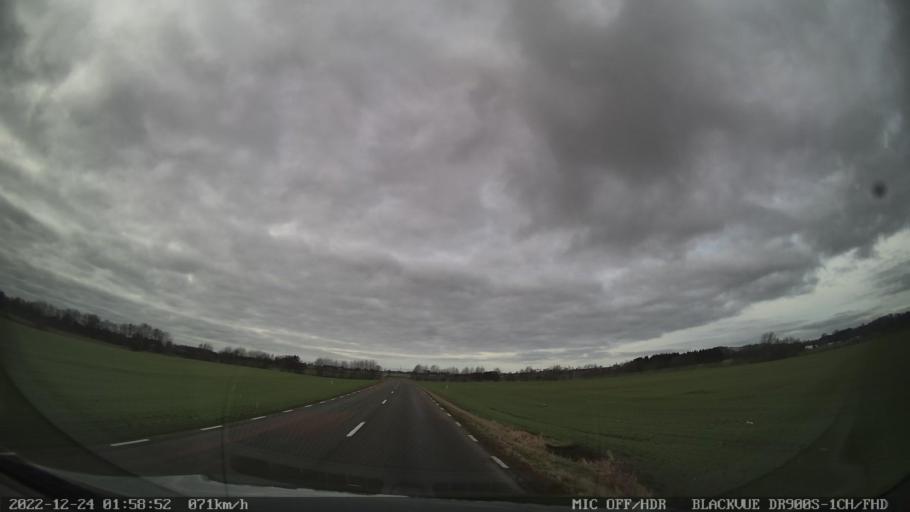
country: SE
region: Skane
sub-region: Tomelilla Kommun
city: Tomelilla
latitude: 55.6054
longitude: 14.0249
